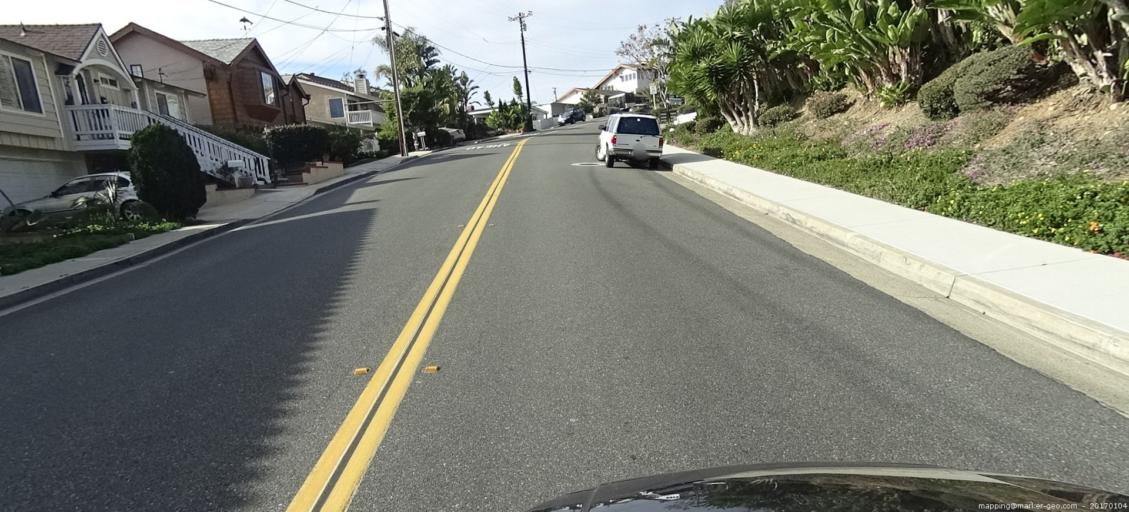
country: US
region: California
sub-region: Orange County
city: Dana Point
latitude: 33.4694
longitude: -117.6892
